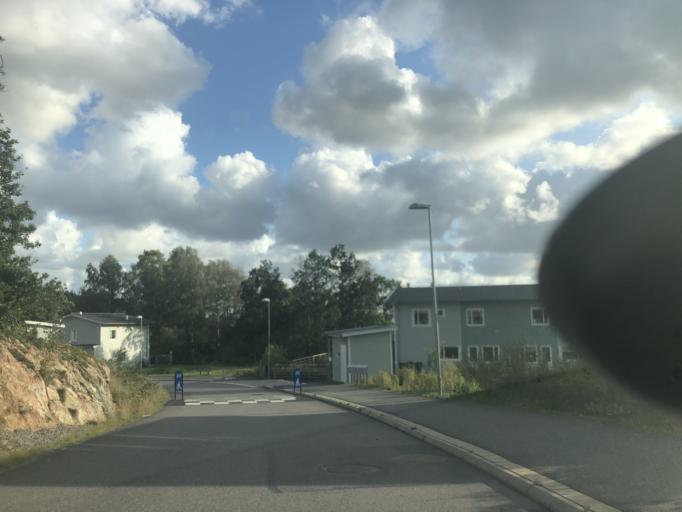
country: SE
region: Vaestra Goetaland
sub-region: Goteborg
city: Goeteborg
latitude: 57.7413
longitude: 11.9615
